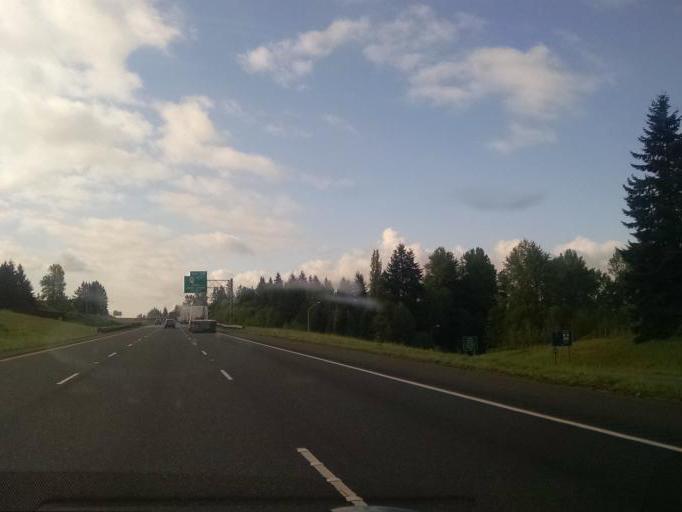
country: US
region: Washington
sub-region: Cowlitz County
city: Kelso
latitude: 46.1584
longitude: -122.9027
